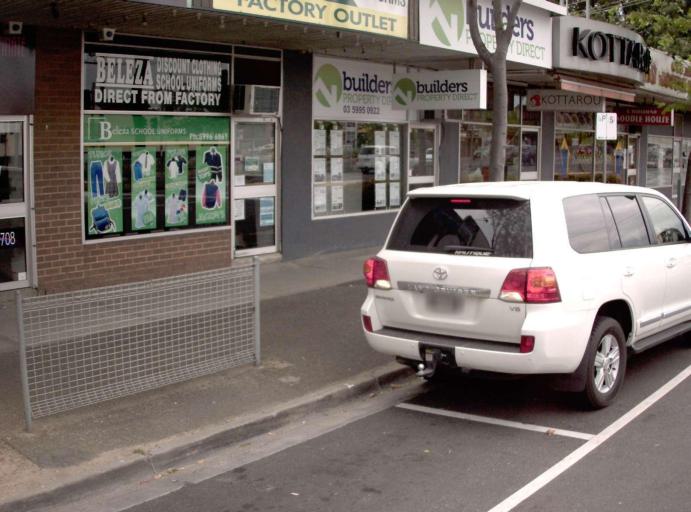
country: AU
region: Victoria
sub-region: Casey
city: Cranbourne
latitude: -38.1090
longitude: 145.2836
